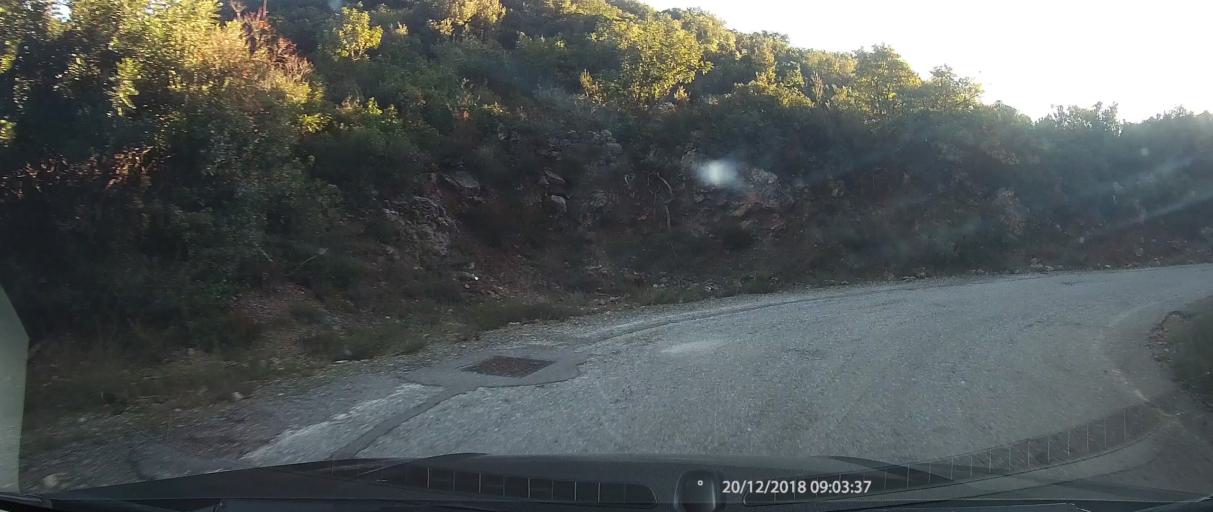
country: GR
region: Peloponnese
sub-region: Nomos Lakonias
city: Sykea
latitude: 36.9522
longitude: 22.9945
